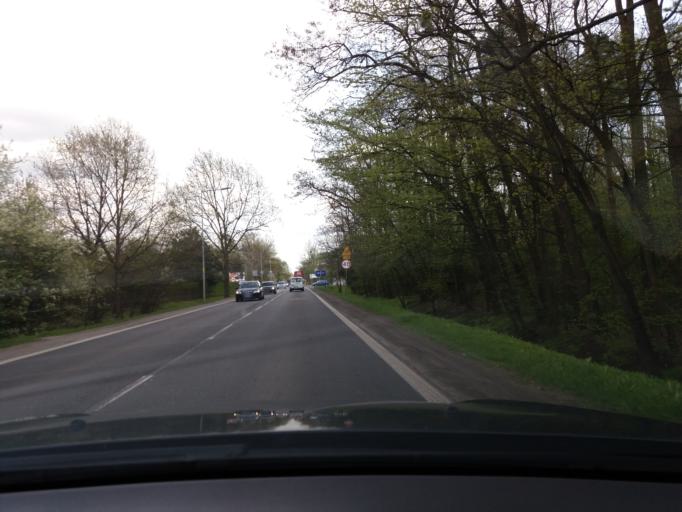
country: PL
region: Lower Silesian Voivodeship
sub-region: Powiat sredzki
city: Mrozow
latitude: 51.1476
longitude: 16.8516
